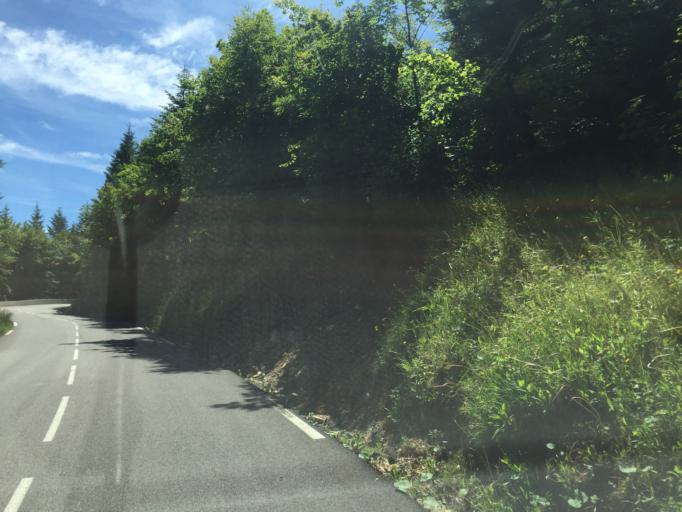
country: FR
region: Rhone-Alpes
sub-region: Departement de la Savoie
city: Saint-Baldoph
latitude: 45.4905
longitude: 5.9193
